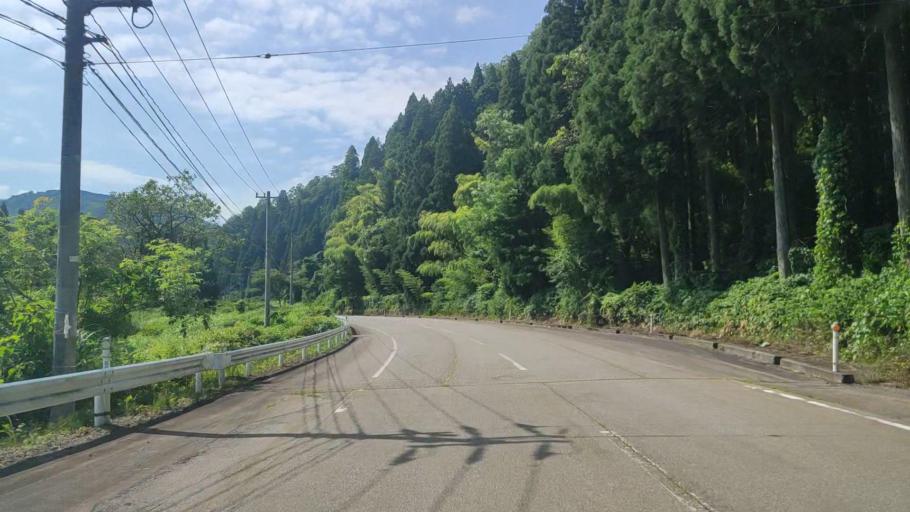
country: JP
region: Ishikawa
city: Komatsu
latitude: 36.3257
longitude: 136.5290
